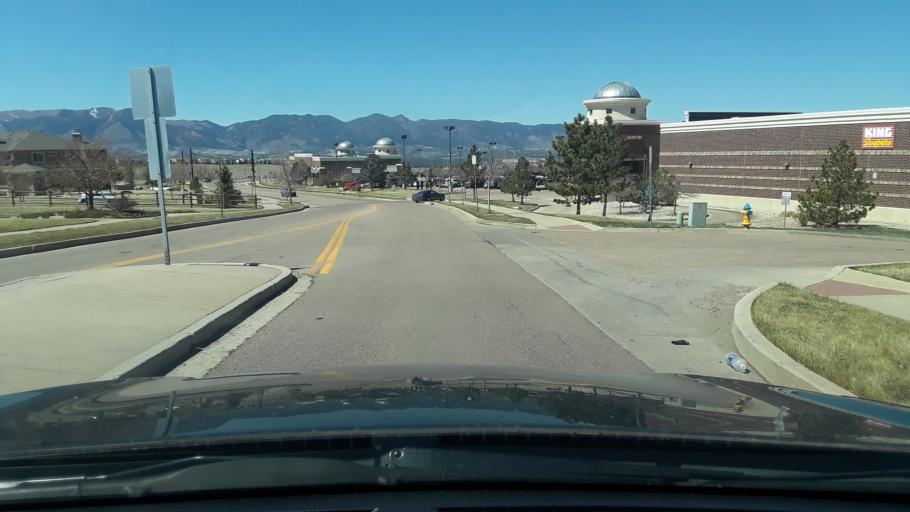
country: US
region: Colorado
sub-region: El Paso County
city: Black Forest
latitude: 38.9637
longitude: -104.7546
